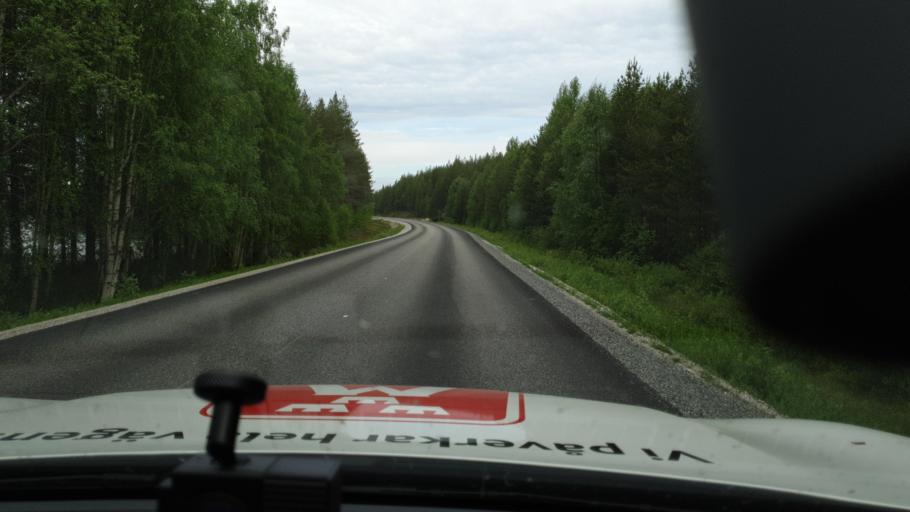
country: SE
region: Vaesterbotten
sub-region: Mala Kommun
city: Mala
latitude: 64.9121
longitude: 18.6584
